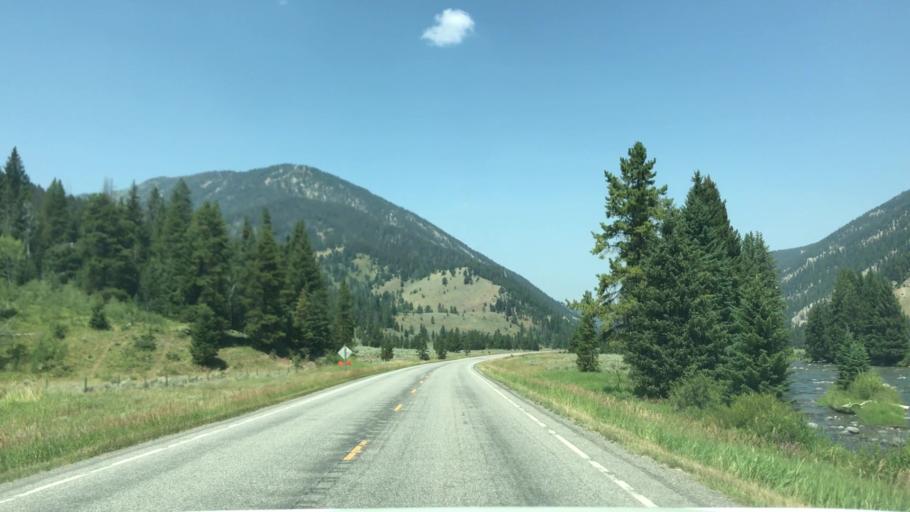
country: US
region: Montana
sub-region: Gallatin County
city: Big Sky
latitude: 45.1026
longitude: -111.2198
